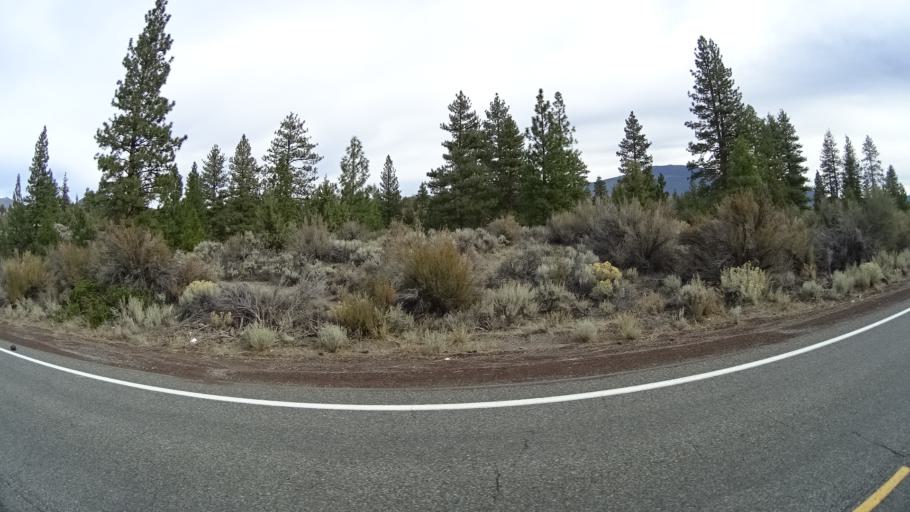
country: US
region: California
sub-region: Siskiyou County
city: Weed
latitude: 41.5370
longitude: -122.2437
